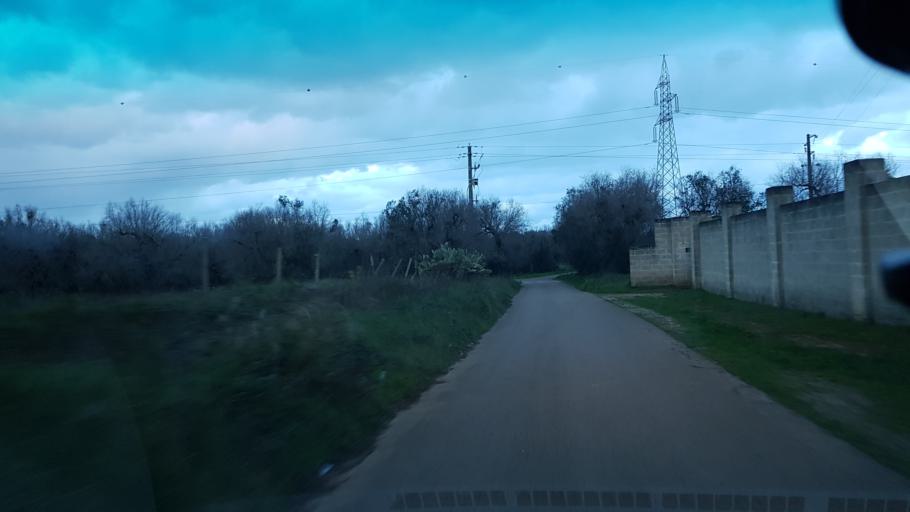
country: IT
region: Apulia
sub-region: Provincia di Brindisi
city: Torchiarolo
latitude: 40.4879
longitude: 18.0581
